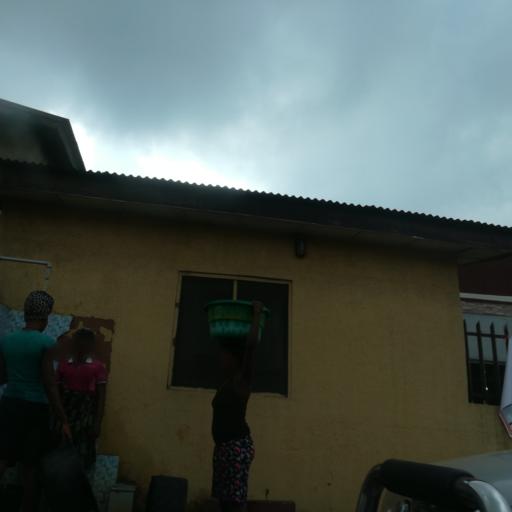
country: NG
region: Lagos
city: Oshodi
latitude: 6.5813
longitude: 3.3067
